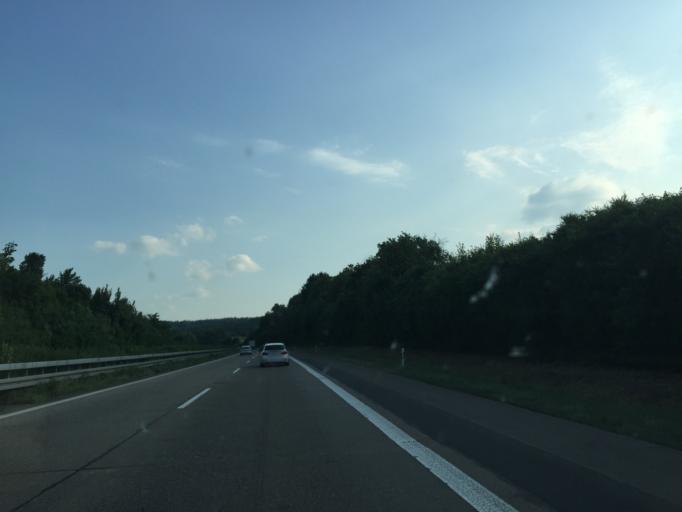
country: DE
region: Baden-Wuerttemberg
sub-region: Regierungsbezirk Stuttgart
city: Neuenstadt am Kocher
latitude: 49.2154
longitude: 9.3465
